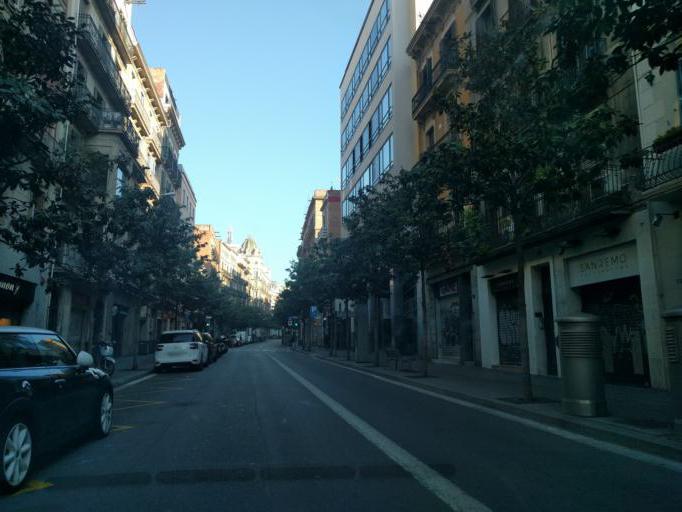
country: ES
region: Catalonia
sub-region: Provincia de Barcelona
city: Gracia
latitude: 41.4010
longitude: 2.1541
